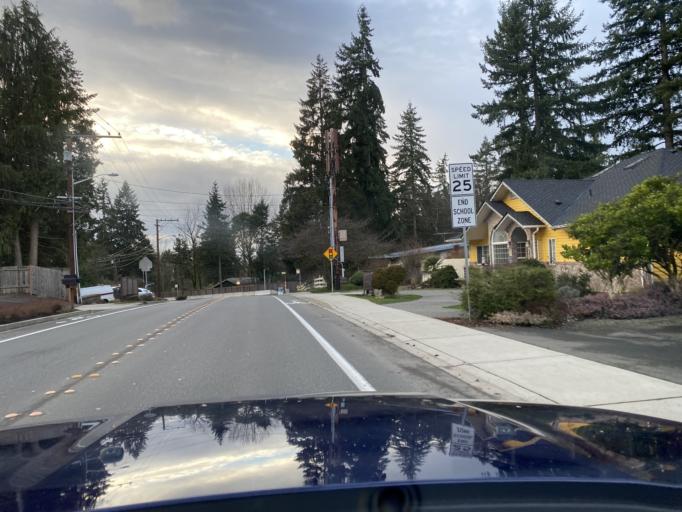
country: US
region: Washington
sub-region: King County
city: Eastgate
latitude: 47.5714
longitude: -122.1392
